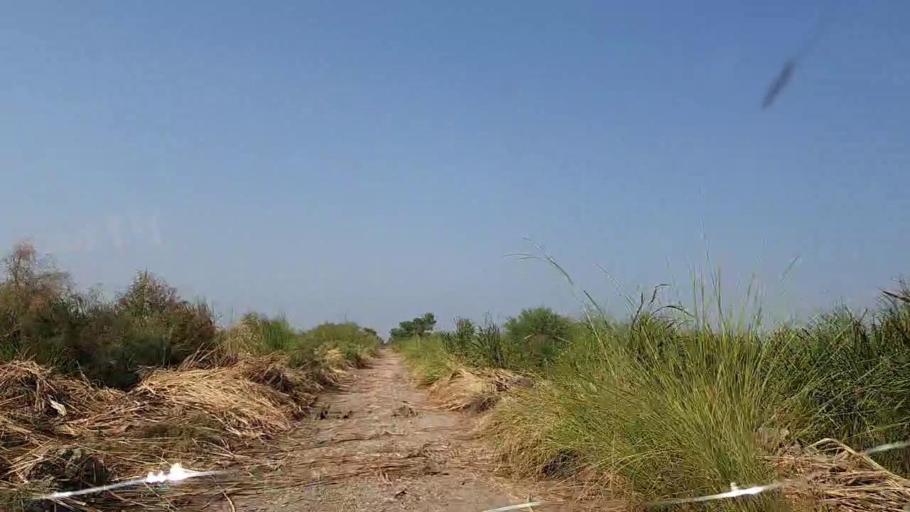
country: PK
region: Sindh
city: Khanpur
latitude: 27.6800
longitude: 69.3777
